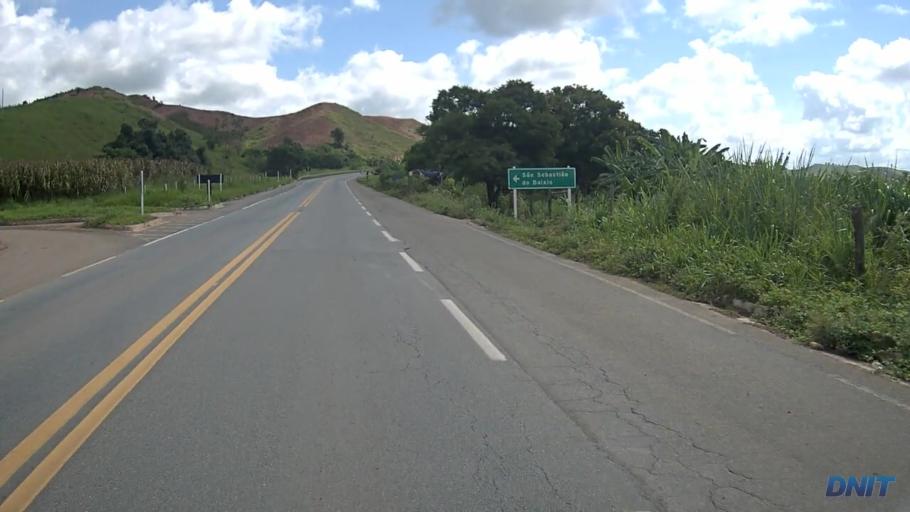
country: BR
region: Minas Gerais
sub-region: Belo Oriente
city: Belo Oriente
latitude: -19.1493
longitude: -42.2325
